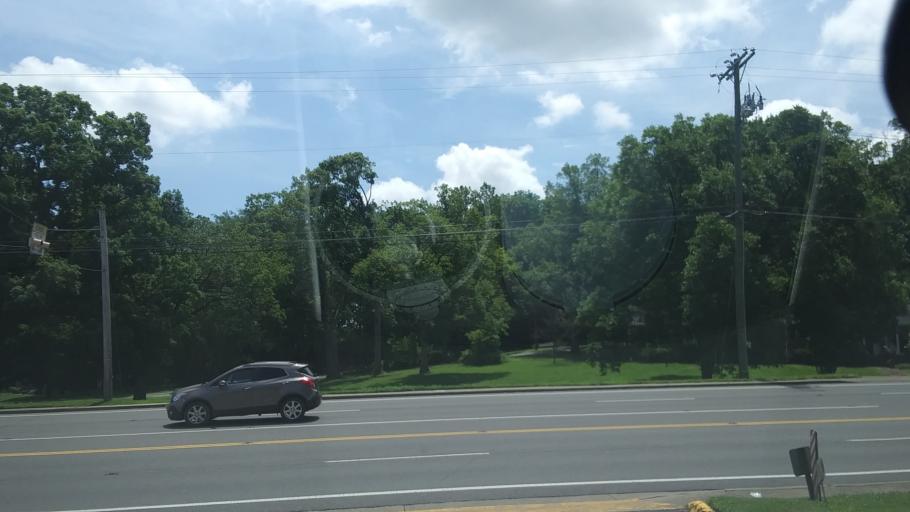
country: US
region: Tennessee
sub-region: Rutherford County
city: La Vergne
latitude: 36.0630
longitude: -86.6378
